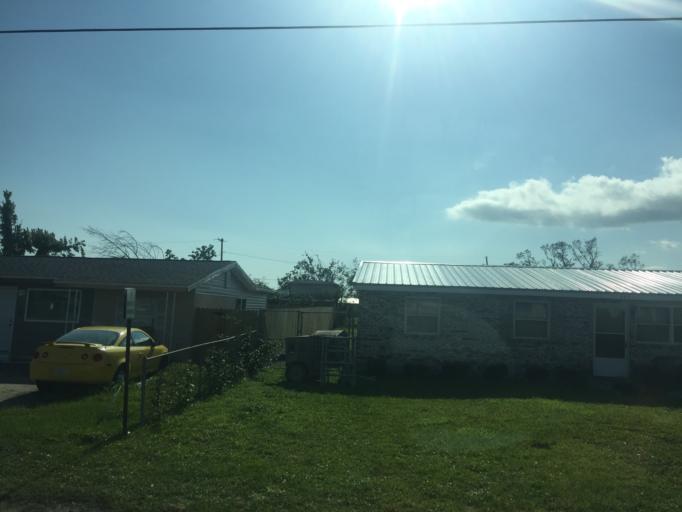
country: US
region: Florida
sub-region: Bay County
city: Cedar Grove
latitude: 30.1648
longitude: -85.6165
